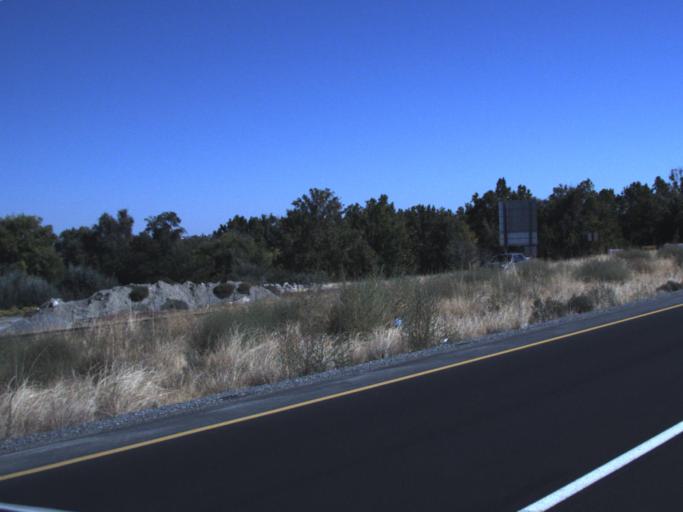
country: US
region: Washington
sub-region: Franklin County
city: West Pasco
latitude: 46.2322
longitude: -119.2156
